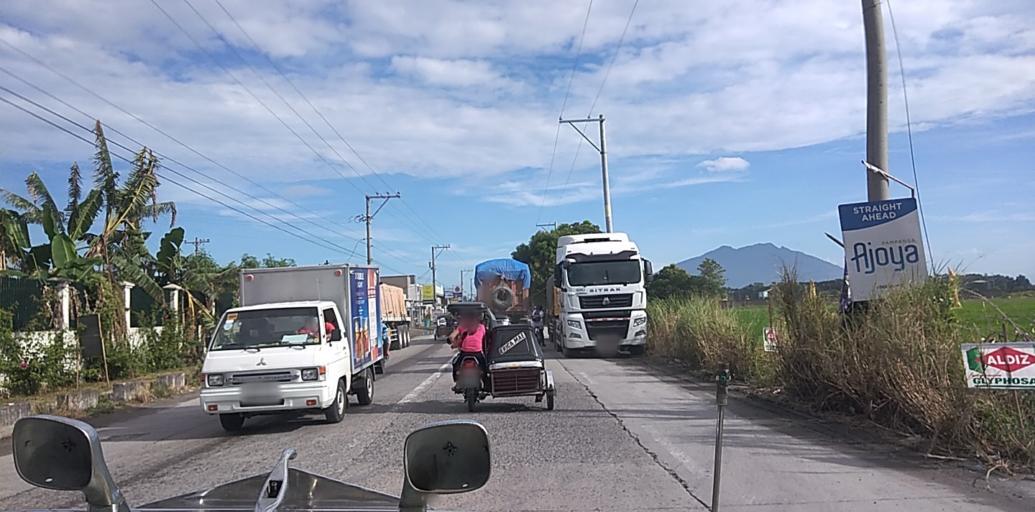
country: PH
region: Central Luzon
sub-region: Province of Pampanga
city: Bulaon
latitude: 15.1005
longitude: 120.6579
